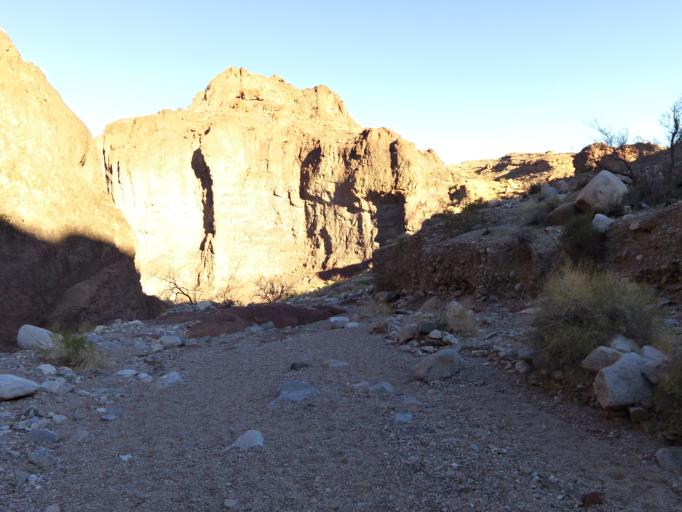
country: US
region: Nevada
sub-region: Clark County
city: Boulder City
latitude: 35.9742
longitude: -114.7107
